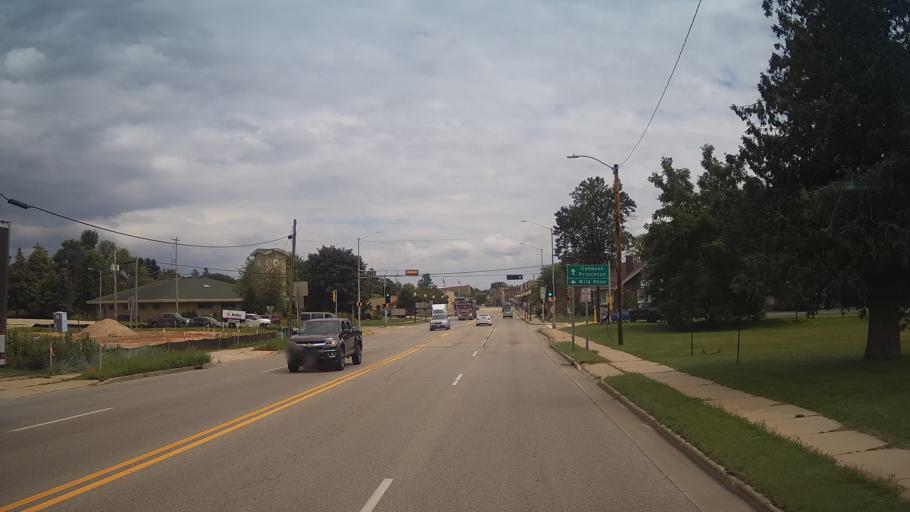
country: US
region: Wisconsin
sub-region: Waushara County
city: Wautoma
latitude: 44.0762
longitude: -89.2946
